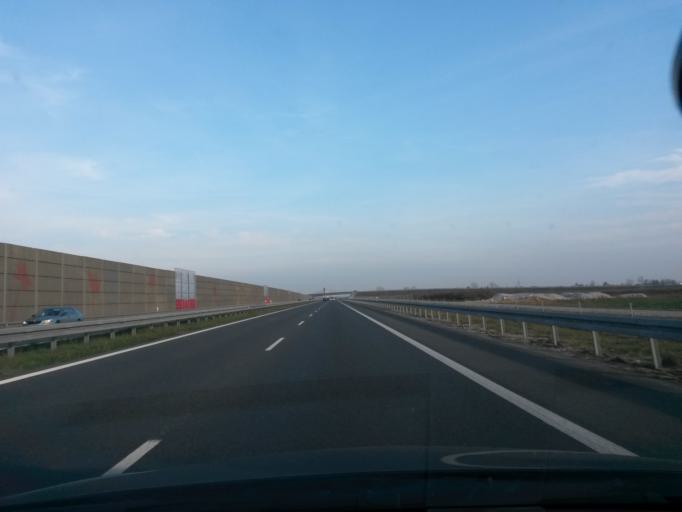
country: PL
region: Lower Silesian Voivodeship
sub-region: Powiat olesnicki
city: Olesnica
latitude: 51.2257
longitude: 17.3513
